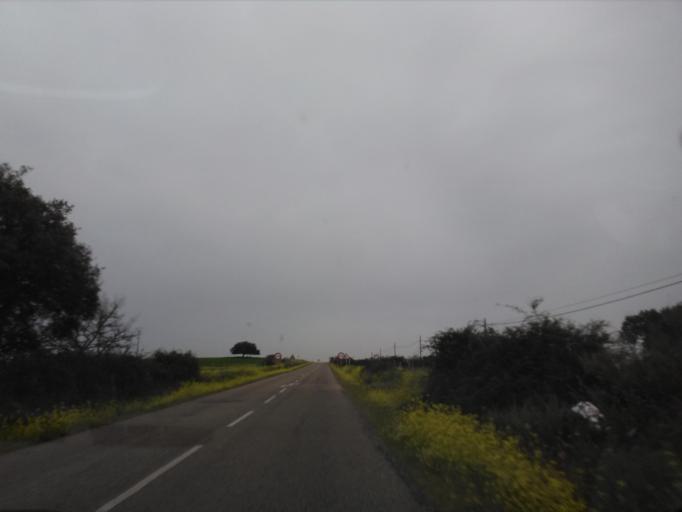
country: ES
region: Castille and Leon
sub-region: Provincia de Salamanca
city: Yecla de Yeltes
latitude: 40.9753
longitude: -6.4730
